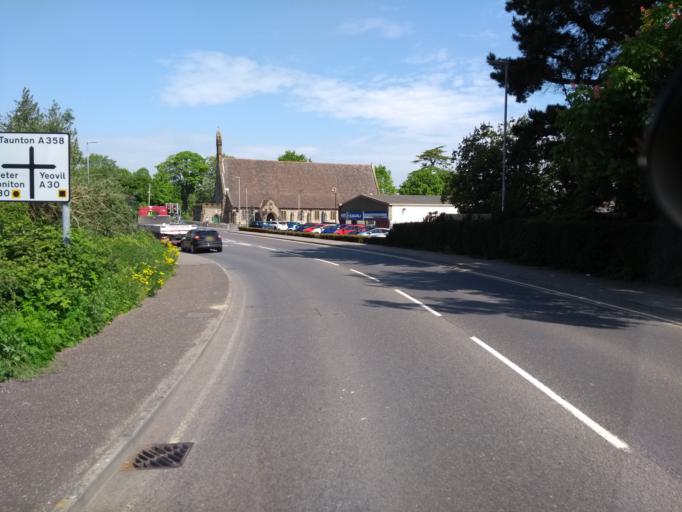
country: GB
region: England
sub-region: Somerset
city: Chard
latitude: 50.8730
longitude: -2.9595
